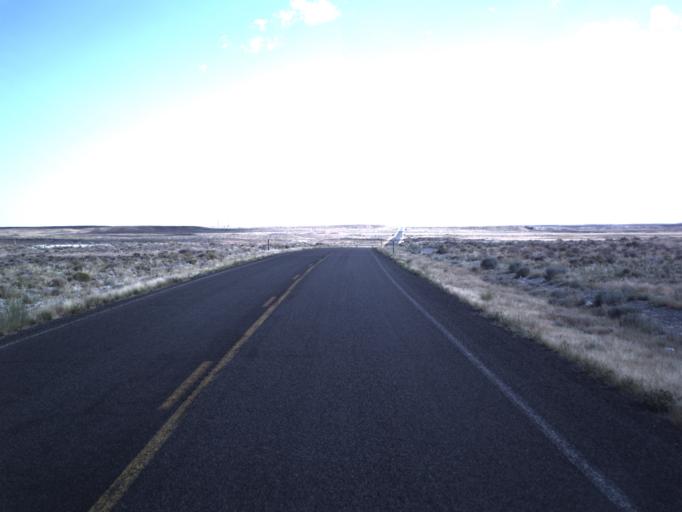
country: US
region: Utah
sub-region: Millard County
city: Fillmore
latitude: 38.8846
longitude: -112.8305
